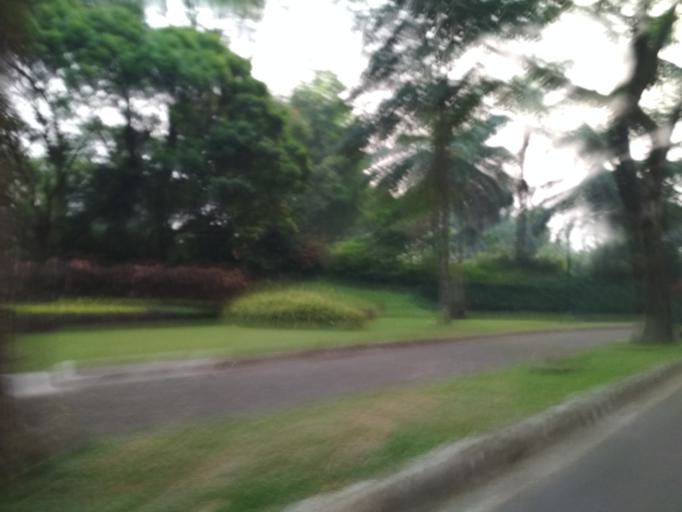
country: ID
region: West Java
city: Caringin
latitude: -6.6628
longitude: 106.8410
